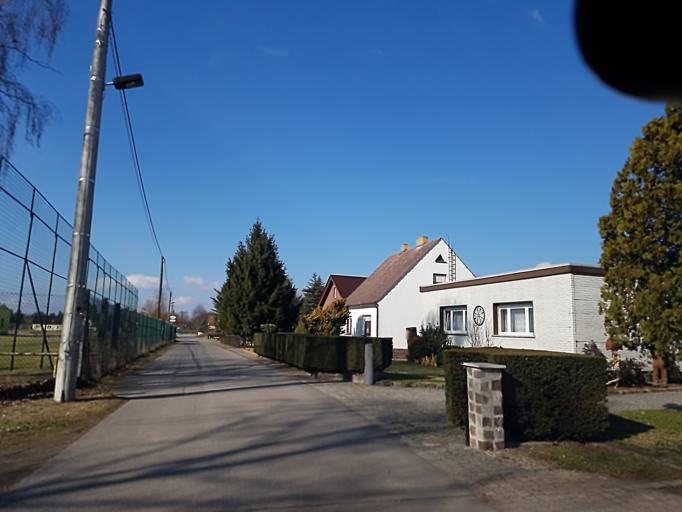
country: DE
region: Brandenburg
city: Doberlug-Kirchhain
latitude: 51.6061
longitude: 13.5637
